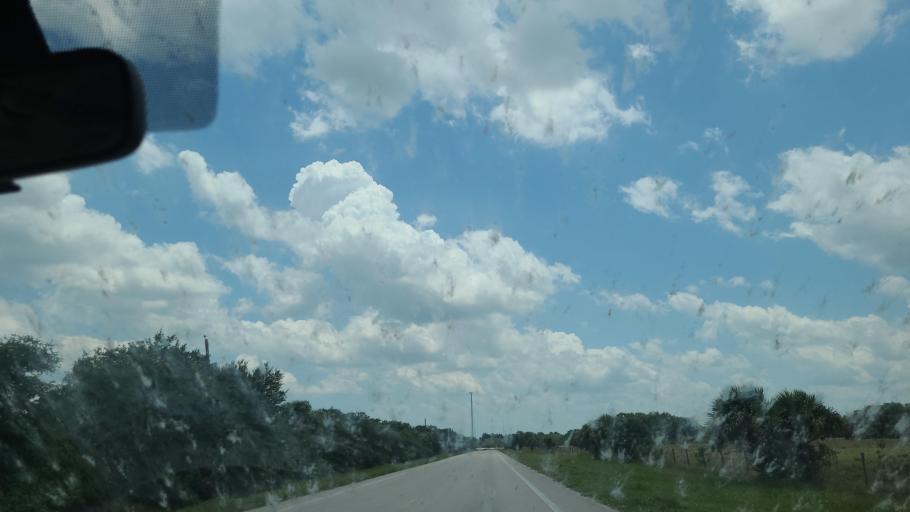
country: US
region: Florida
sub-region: Glades County
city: Buckhead Ridge
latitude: 27.1305
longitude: -81.0877
